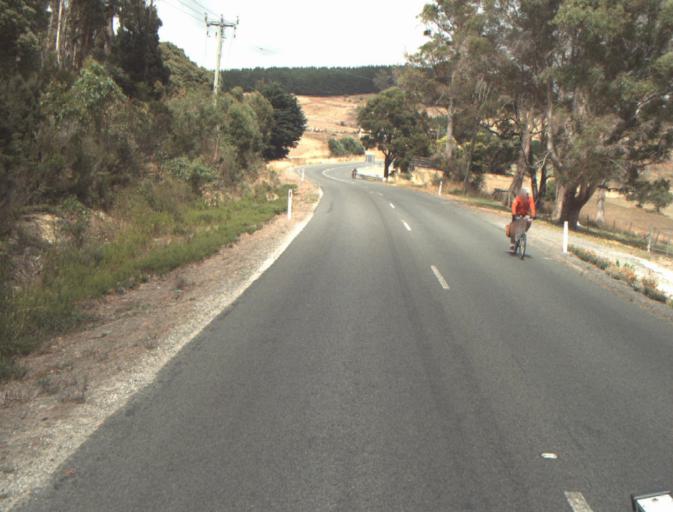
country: AU
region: Tasmania
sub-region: Dorset
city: Bridport
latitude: -41.1633
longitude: 147.2408
